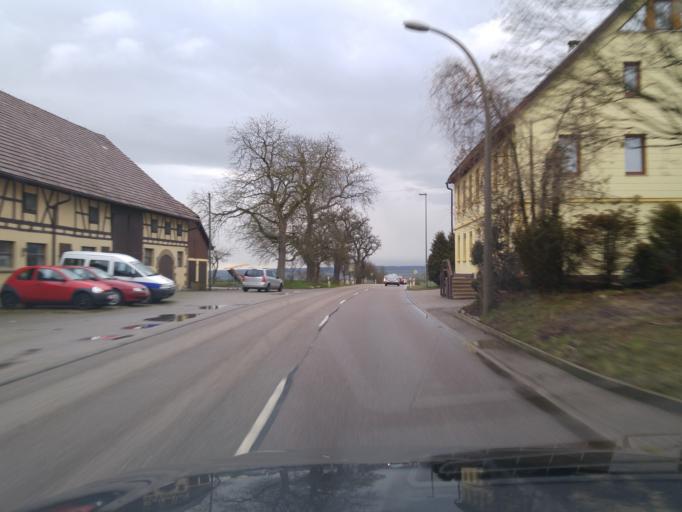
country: DE
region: Baden-Wuerttemberg
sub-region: Regierungsbezirk Stuttgart
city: Bretzfeld
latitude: 49.2262
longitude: 9.4475
